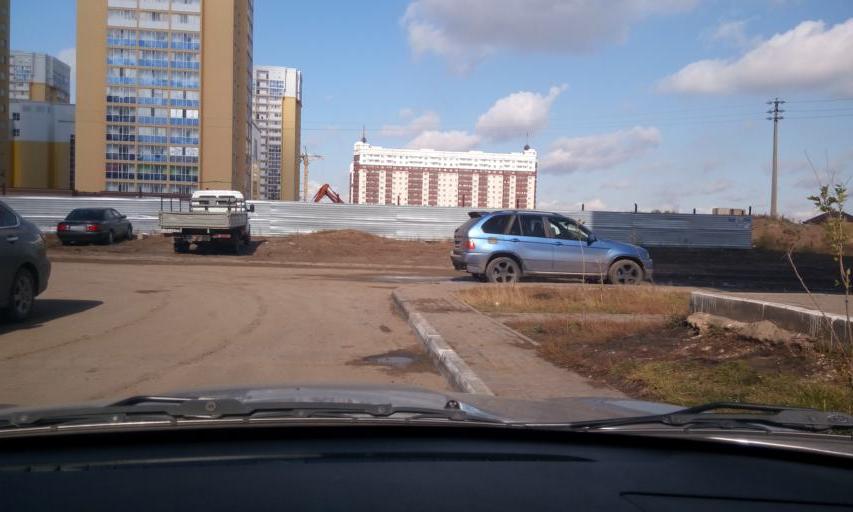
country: KZ
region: Astana Qalasy
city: Astana
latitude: 51.1281
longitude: 71.5058
